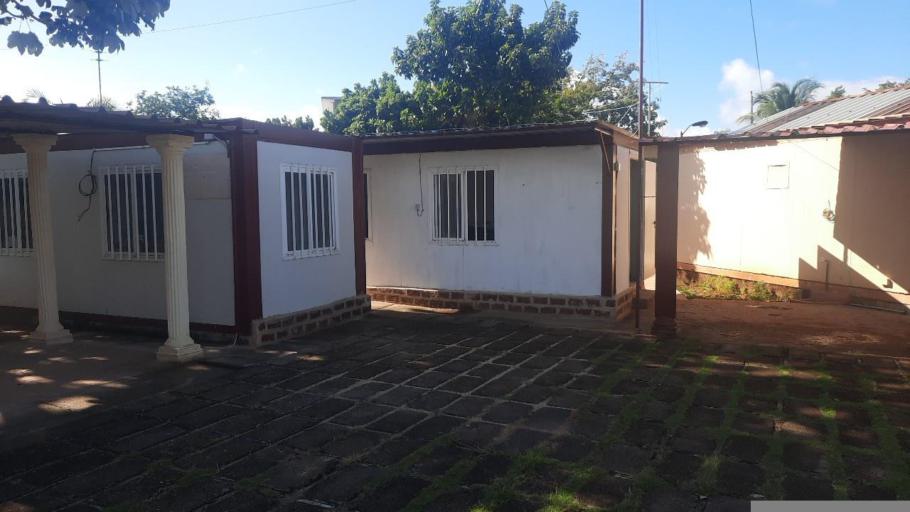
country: CU
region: Matanzas
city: Varadero
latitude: 23.1266
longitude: -81.2907
